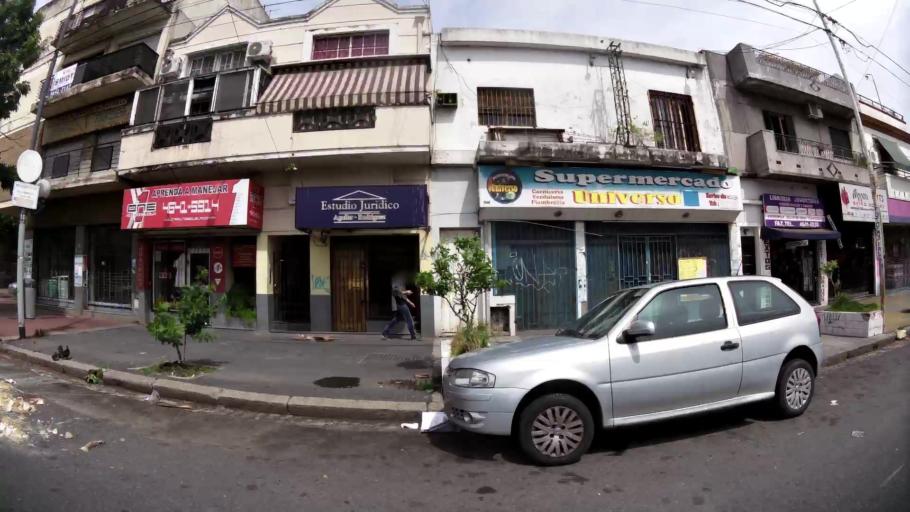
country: AR
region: Buenos Aires
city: Caseros
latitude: -34.6167
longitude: -58.5285
